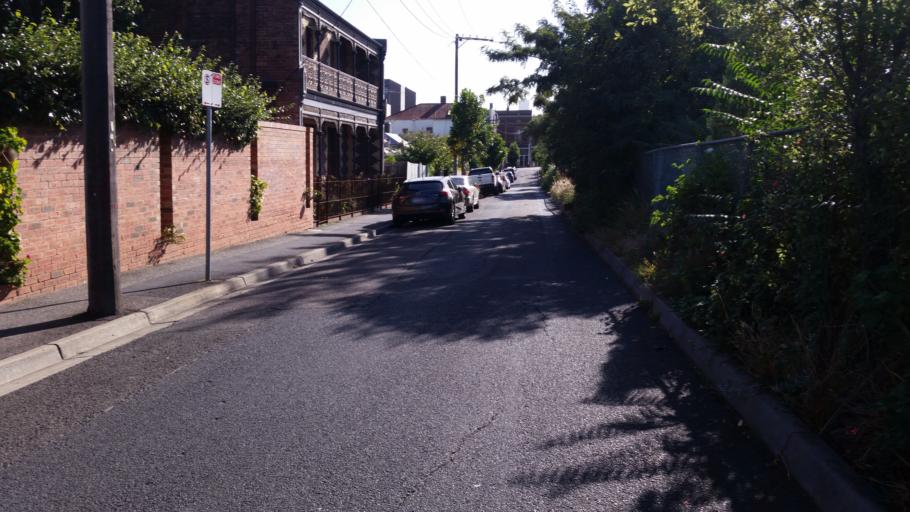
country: AU
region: Victoria
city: Albert Park
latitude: -37.8268
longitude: 144.9992
